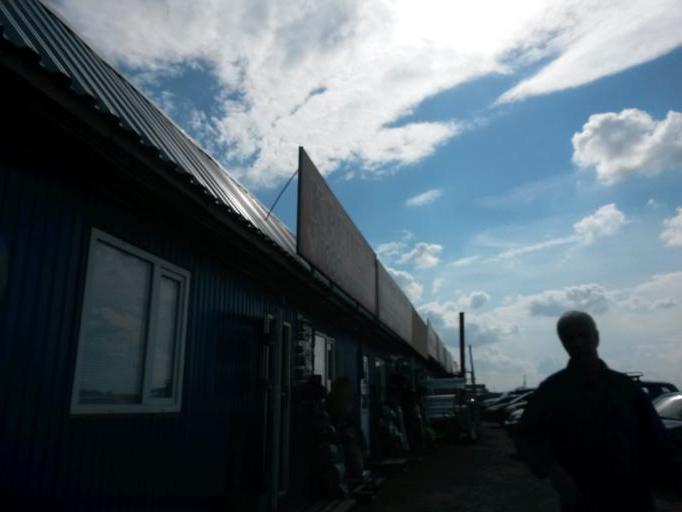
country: RU
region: Moskovskaya
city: Lyubuchany
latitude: 55.2540
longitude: 37.5976
